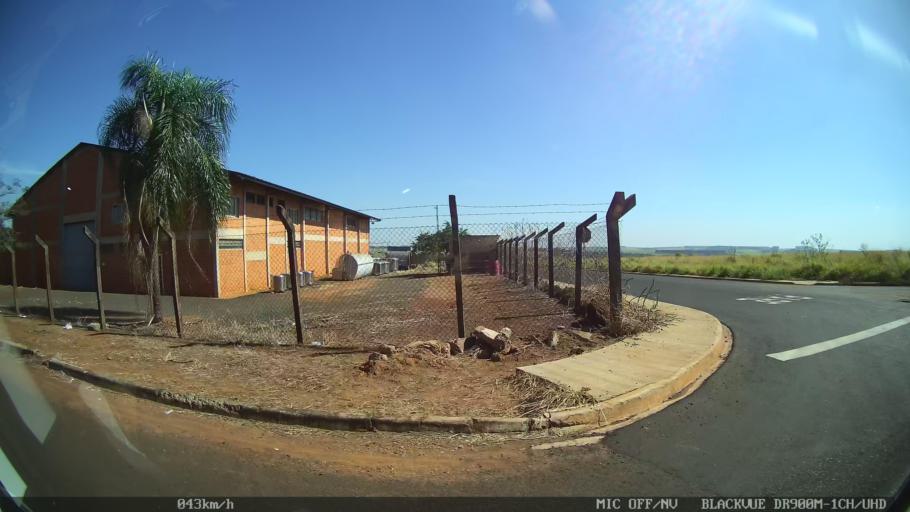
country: BR
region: Sao Paulo
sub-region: Batatais
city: Batatais
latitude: -20.8797
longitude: -47.6015
